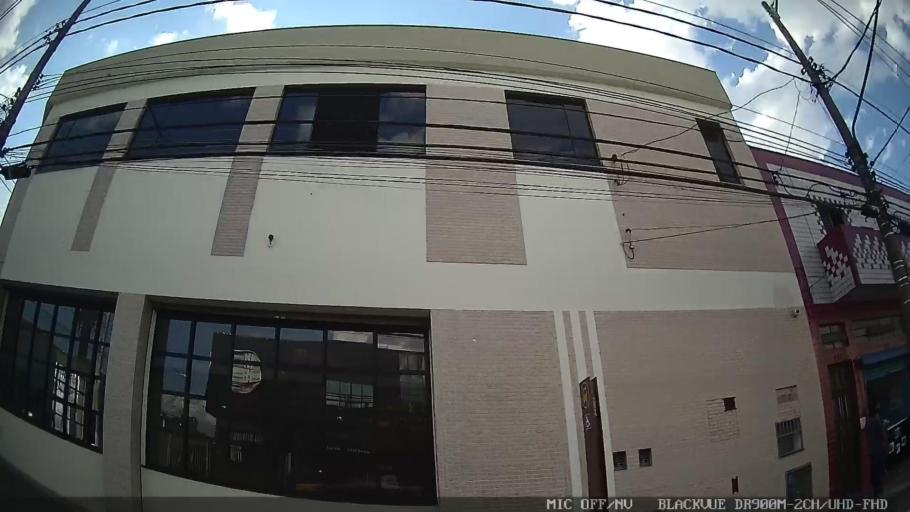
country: BR
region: Sao Paulo
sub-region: Sao Caetano Do Sul
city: Sao Caetano do Sul
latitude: -23.5476
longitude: -46.5495
